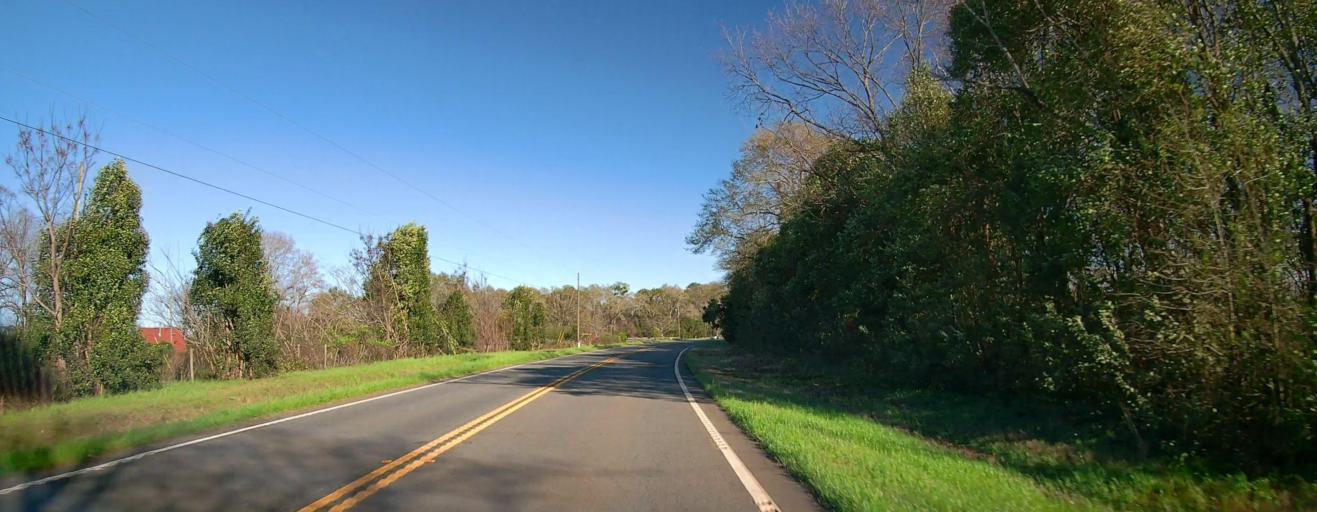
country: US
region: Georgia
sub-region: Macon County
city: Marshallville
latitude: 32.4556
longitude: -83.9168
